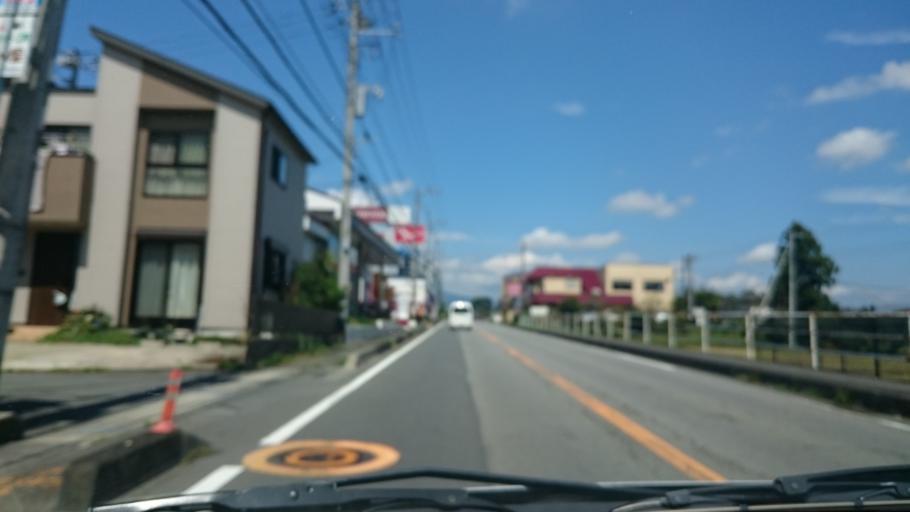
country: JP
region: Shizuoka
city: Gotemba
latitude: 35.2664
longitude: 138.9245
